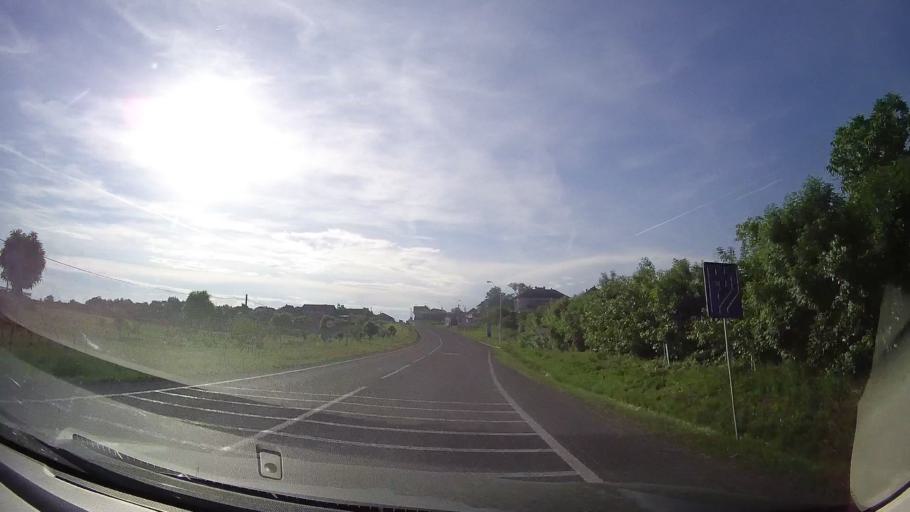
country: RO
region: Timis
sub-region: Oras Recas
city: Recas
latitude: 45.7984
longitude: 21.5175
